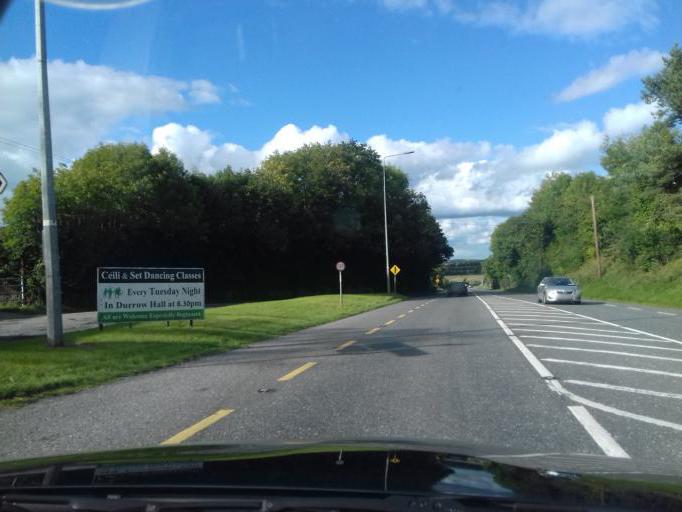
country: IE
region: Leinster
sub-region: An Iarmhi
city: Kilbeggan
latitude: 53.3307
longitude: -7.5122
